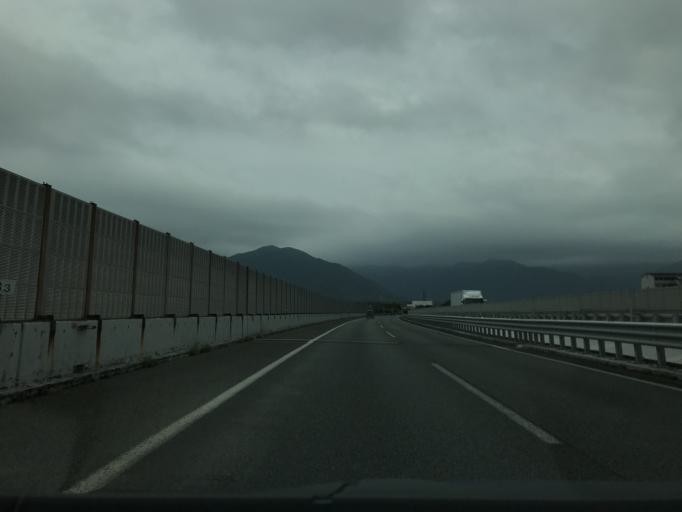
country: JP
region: Fukuoka
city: Nakama
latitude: 33.7833
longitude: 130.7224
